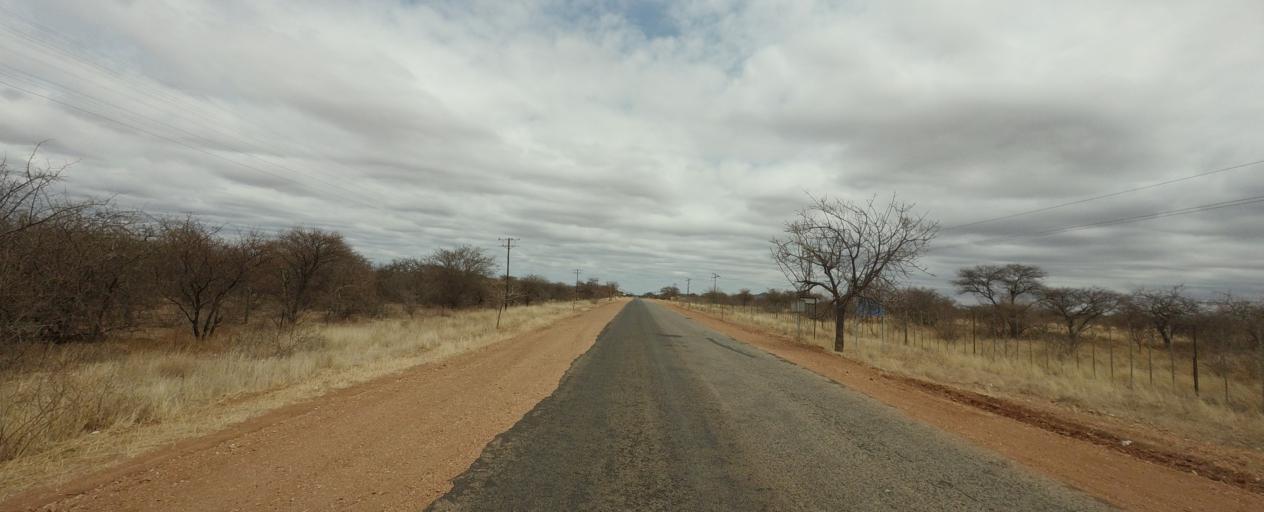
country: BW
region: Central
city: Mathathane
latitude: -22.6772
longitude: 29.0991
